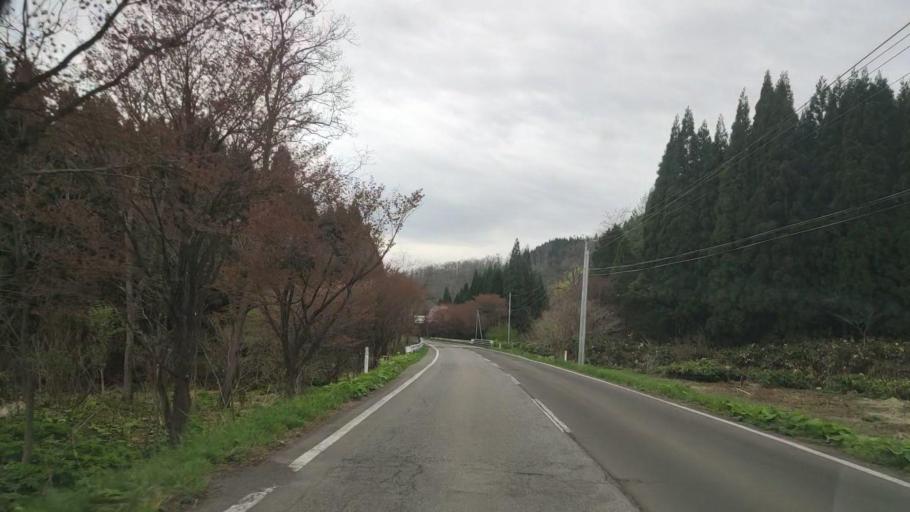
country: JP
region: Akita
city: Hanawa
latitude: 40.3531
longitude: 140.7782
